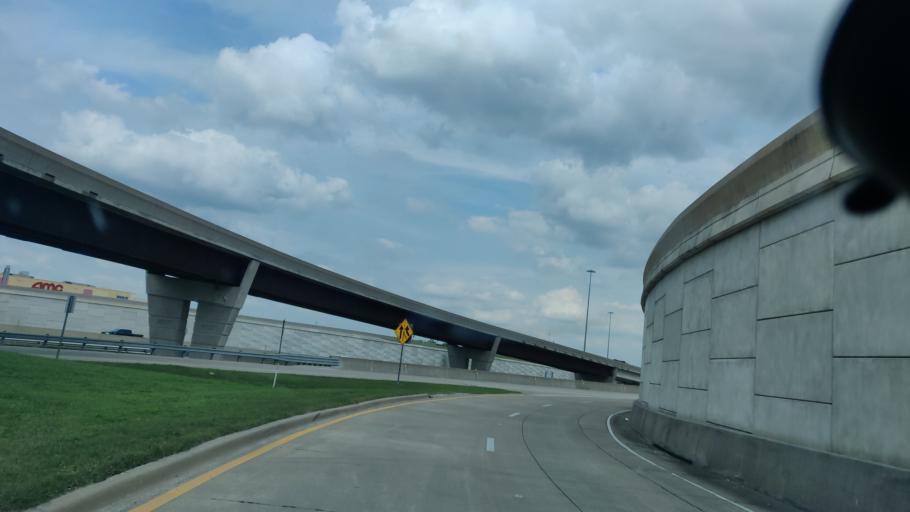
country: US
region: Texas
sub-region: Dallas County
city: Sachse
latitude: 32.9485
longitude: -96.6173
